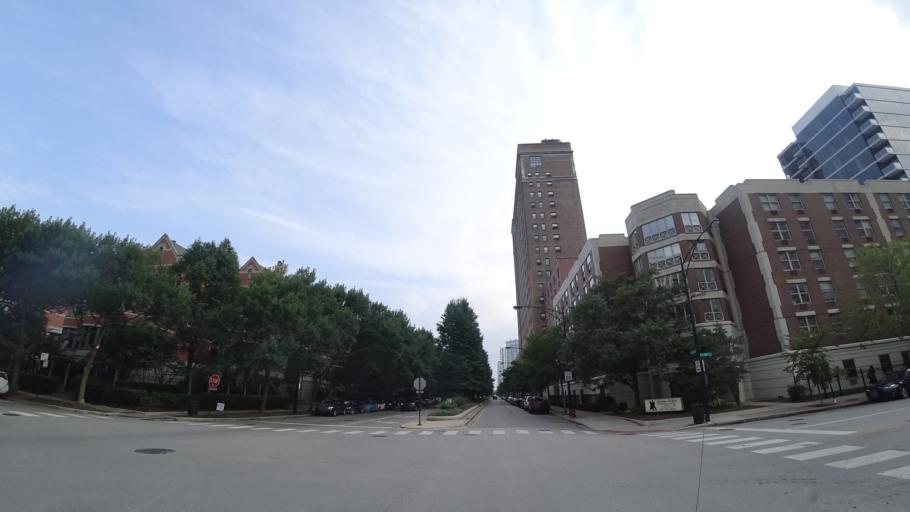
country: US
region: Illinois
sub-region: Cook County
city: Chicago
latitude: 41.8642
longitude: -87.6225
